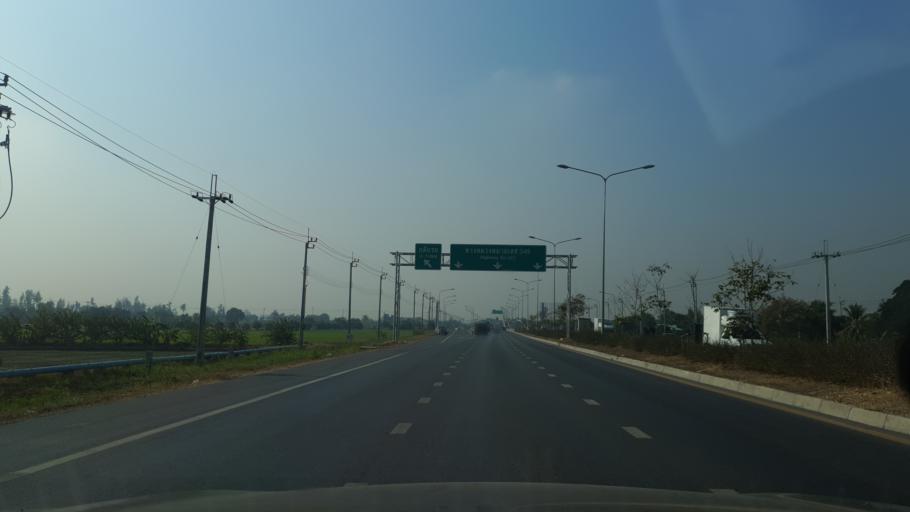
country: TH
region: Nonthaburi
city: Bang Bua Thong
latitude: 13.9677
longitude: 100.4624
